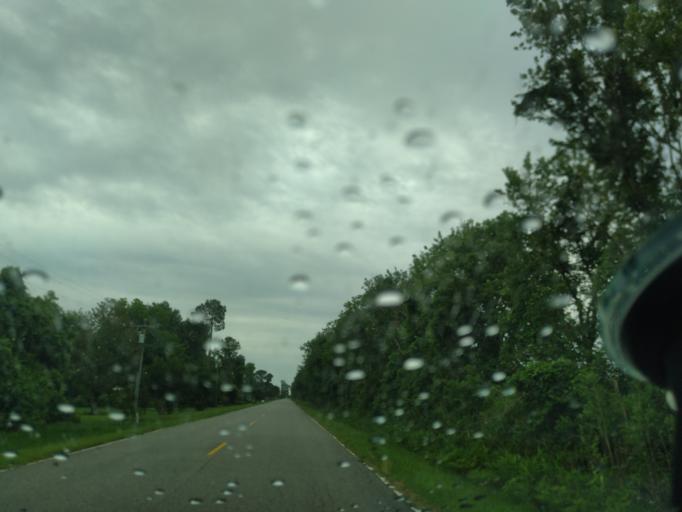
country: US
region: North Carolina
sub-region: Beaufort County
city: Belhaven
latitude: 35.7654
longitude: -76.5245
